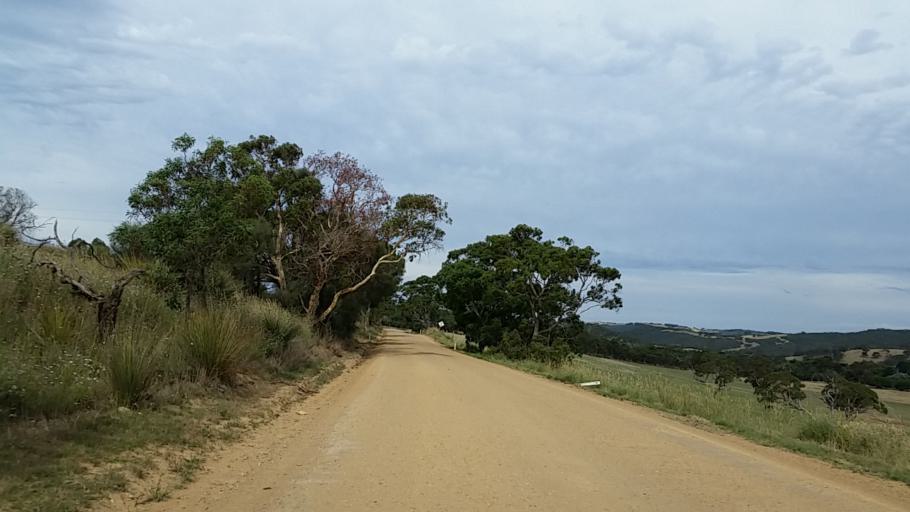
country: AU
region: South Australia
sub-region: Yankalilla
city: Normanville
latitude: -35.4114
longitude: 138.4170
